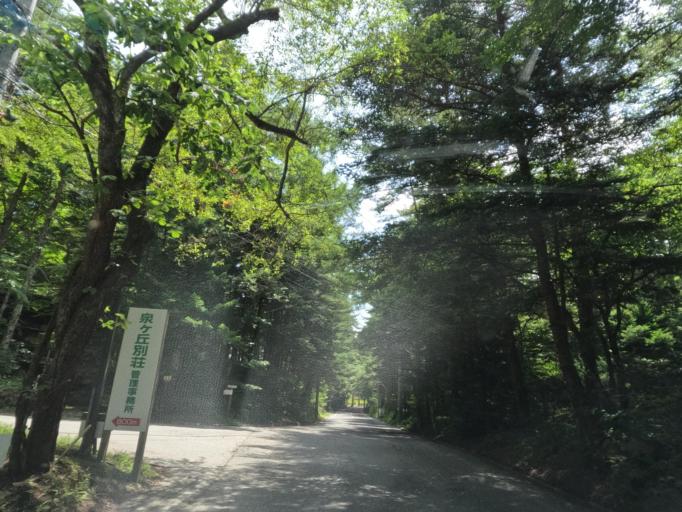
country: JP
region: Nagano
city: Komoro
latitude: 36.3643
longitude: 138.6060
